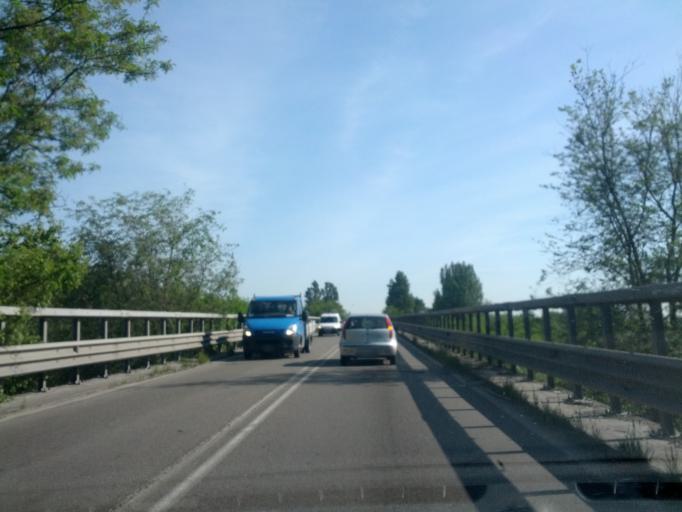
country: IT
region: Emilia-Romagna
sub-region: Provincia di Reggio Emilia
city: Reggio nell'Emilia
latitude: 44.7133
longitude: 10.6203
